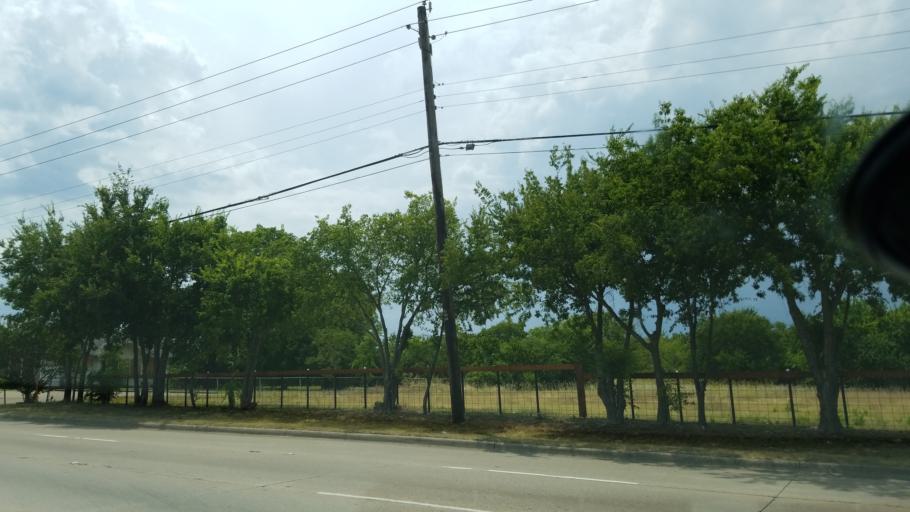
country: US
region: Texas
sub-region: Dallas County
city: Duncanville
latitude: 32.6582
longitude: -96.8571
